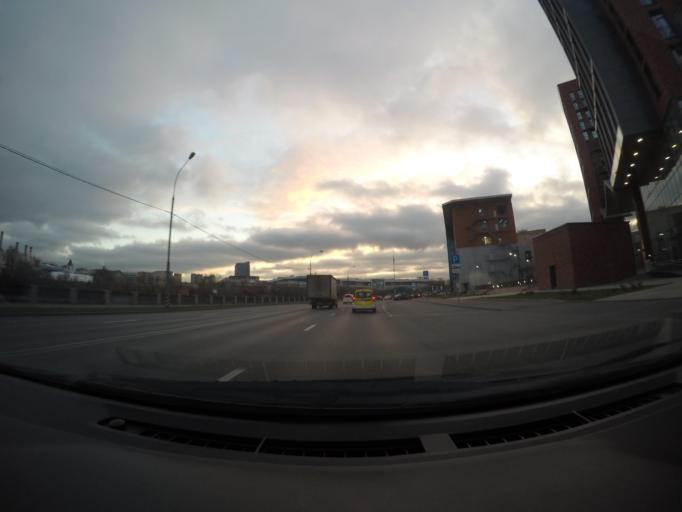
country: RU
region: Moskovskaya
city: Kozhukhovo
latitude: 55.7092
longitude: 37.6473
